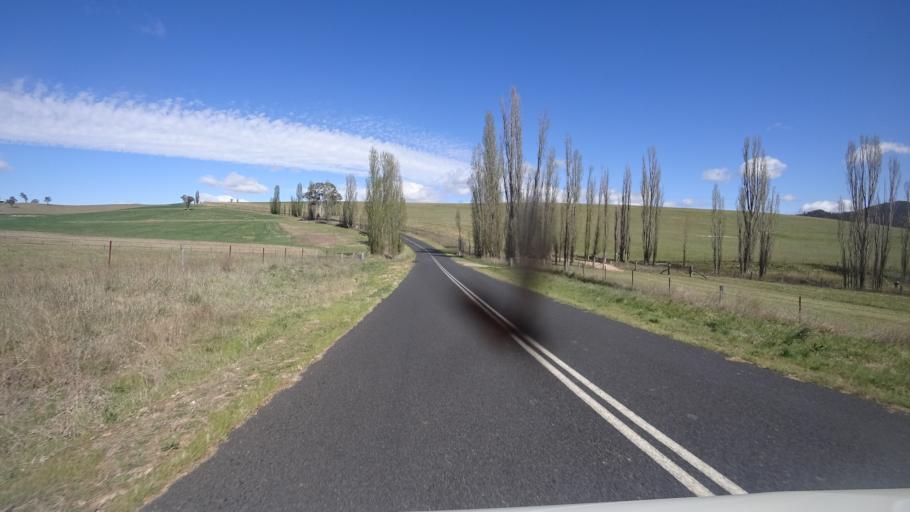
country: AU
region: New South Wales
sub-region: Lithgow
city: Bowenfels
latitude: -33.5169
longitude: 149.9555
